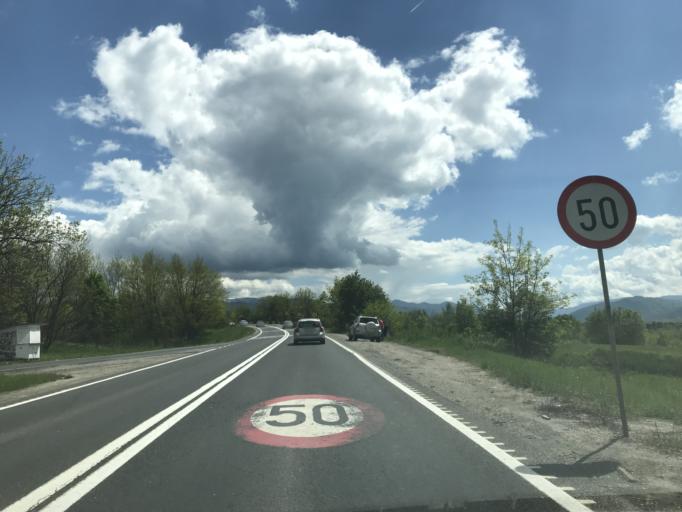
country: RO
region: Sibiu
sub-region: Comuna Talmaciu
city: Talmaciu
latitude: 45.6991
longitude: 24.2694
